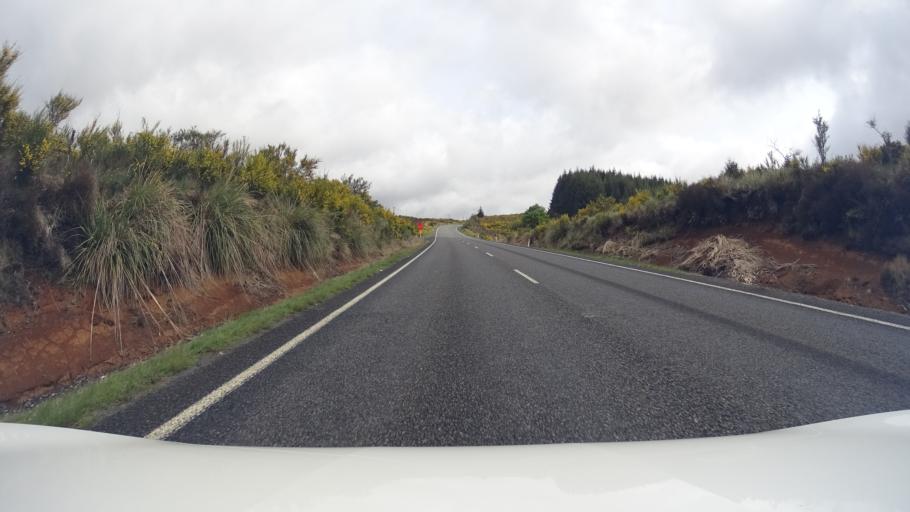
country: NZ
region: Manawatu-Wanganui
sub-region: Ruapehu District
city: Waiouru
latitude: -39.2033
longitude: 175.4025
